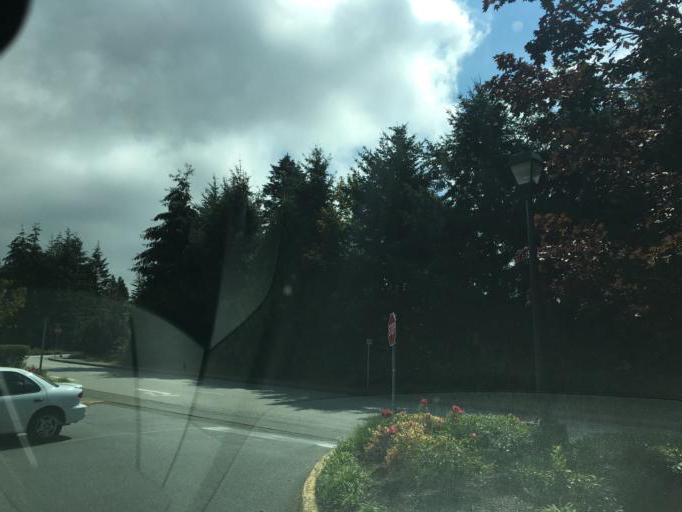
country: CA
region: British Columbia
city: West Vancouver
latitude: 49.3506
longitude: -123.2532
